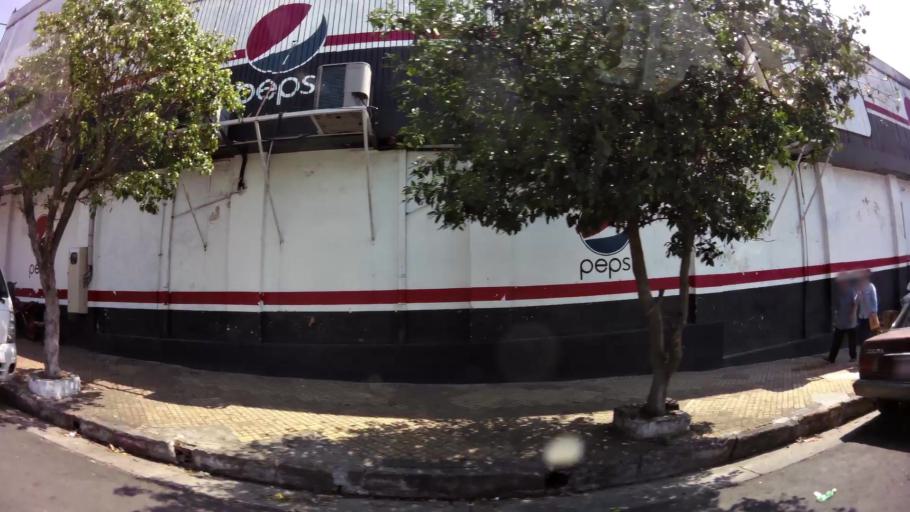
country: PY
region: Presidente Hayes
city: Nanawa
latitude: -25.2827
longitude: -57.6541
